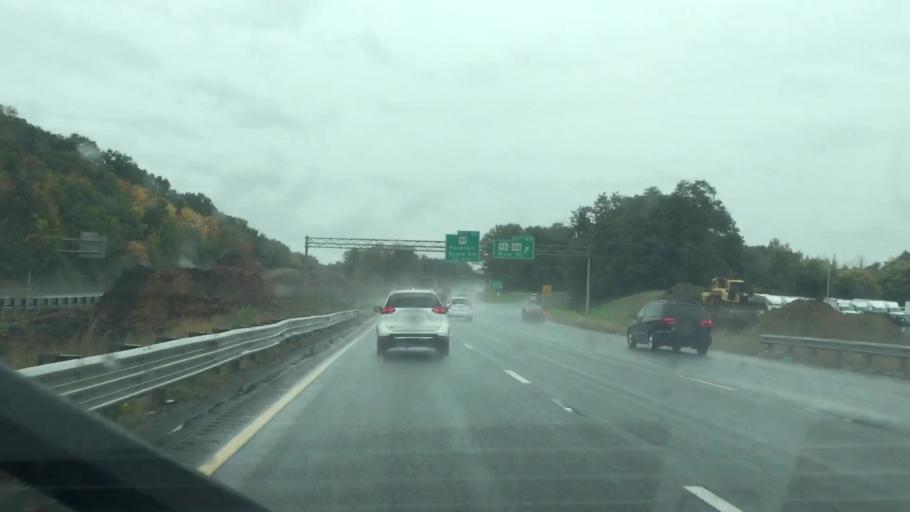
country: US
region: Massachusetts
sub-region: Essex County
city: Haverhill
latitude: 42.7684
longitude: -71.1203
